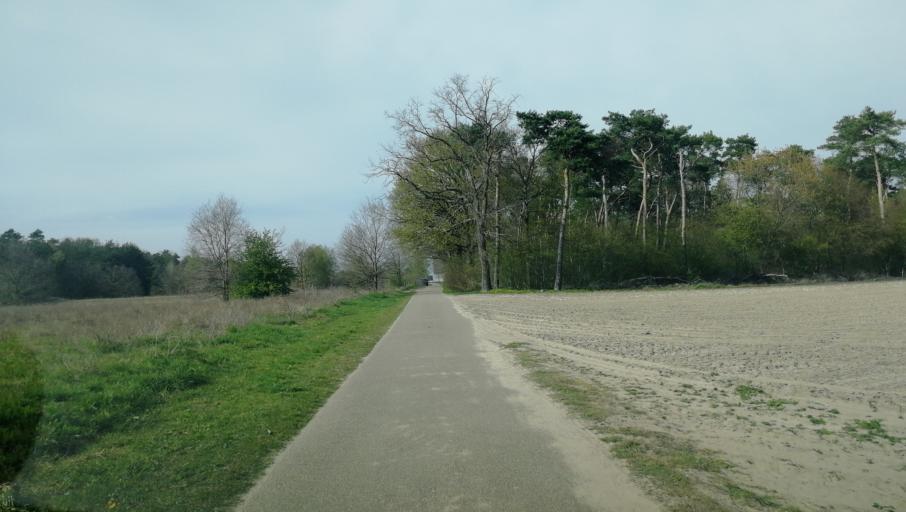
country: NL
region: Limburg
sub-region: Gemeente Peel en Maas
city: Maasbree
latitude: 51.3811
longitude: 6.0920
